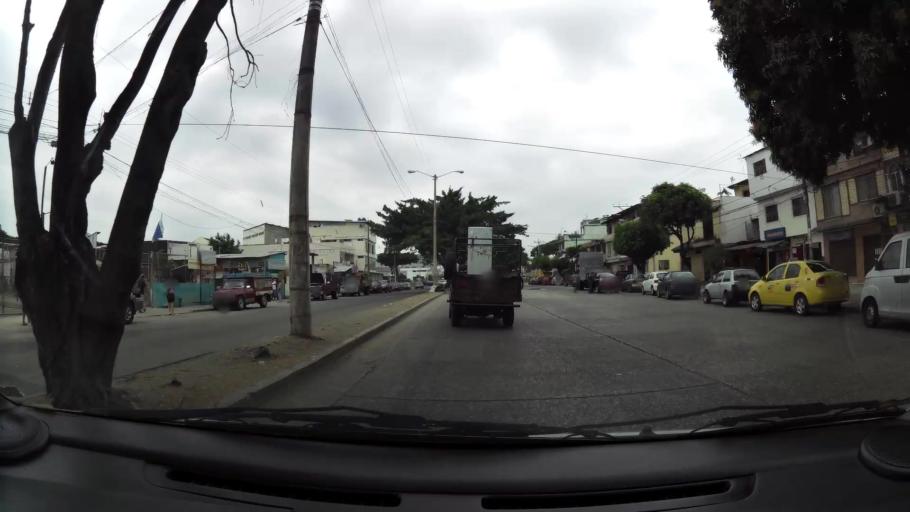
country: EC
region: Guayas
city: Eloy Alfaro
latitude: -2.1311
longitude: -79.8878
